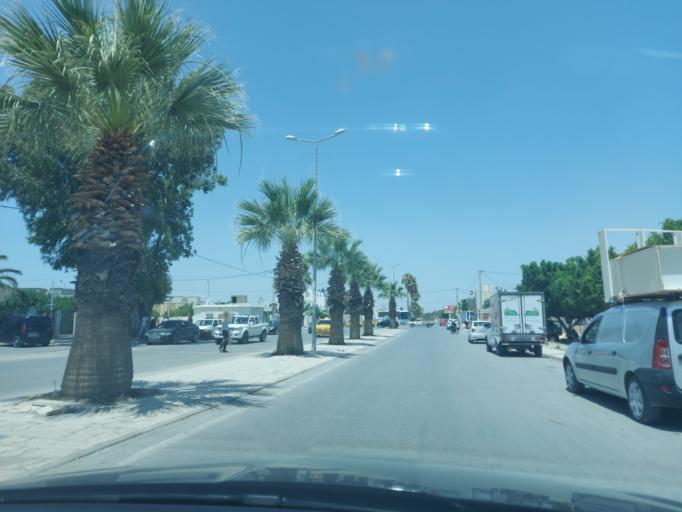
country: TN
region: Silyanah
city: Siliana
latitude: 36.0910
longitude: 9.3718
